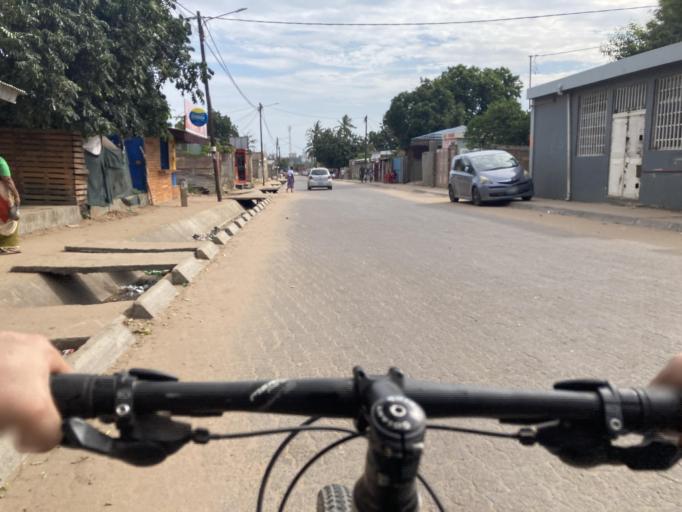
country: MZ
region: Maputo City
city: Maputo
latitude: -25.9370
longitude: 32.5852
